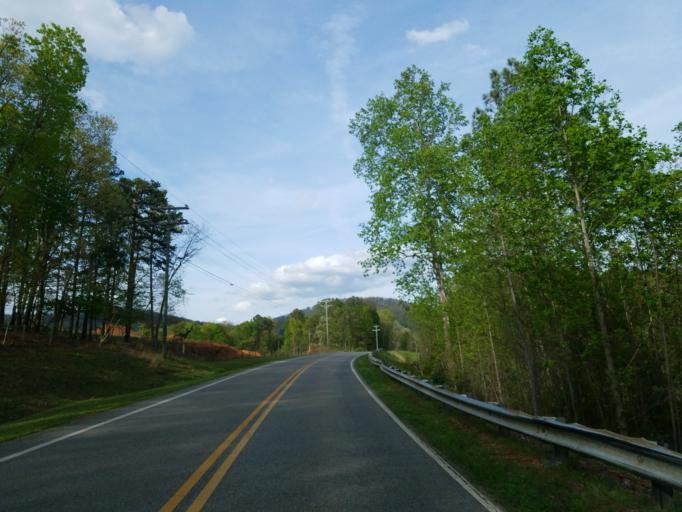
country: US
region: Georgia
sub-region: Pickens County
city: Nelson
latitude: 34.4422
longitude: -84.3251
